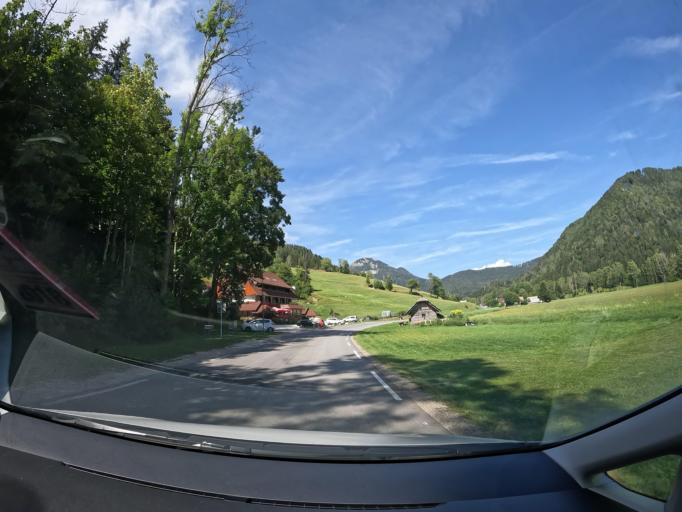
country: AT
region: Carinthia
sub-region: Politischer Bezirk Feldkirchen
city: Feldkirchen in Karnten
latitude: 46.6811
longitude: 14.1245
